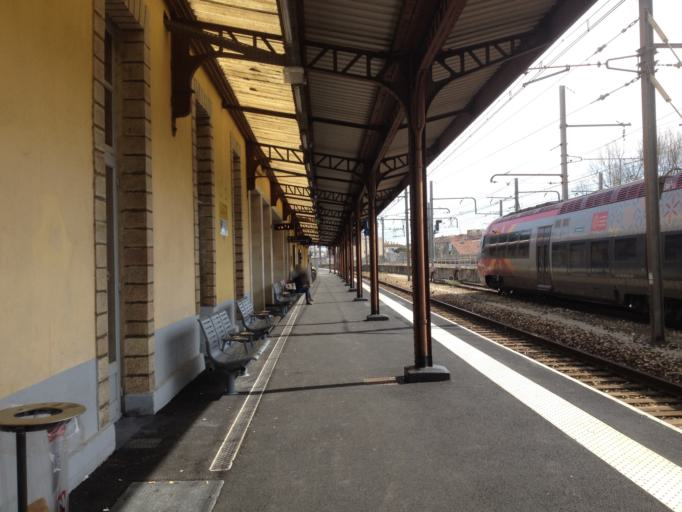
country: FR
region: Provence-Alpes-Cote d'Azur
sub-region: Departement du Vaucluse
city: Avignon
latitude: 43.9414
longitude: 4.8048
